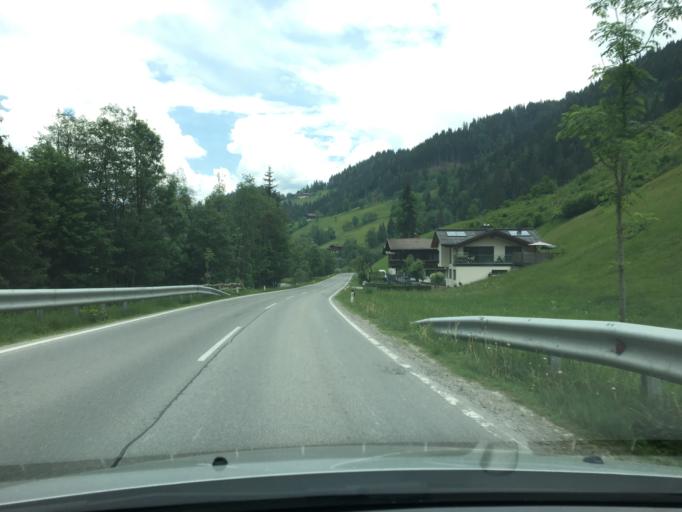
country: AT
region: Salzburg
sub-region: Politischer Bezirk Sankt Johann im Pongau
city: Wagrain
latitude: 47.3144
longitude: 13.3037
